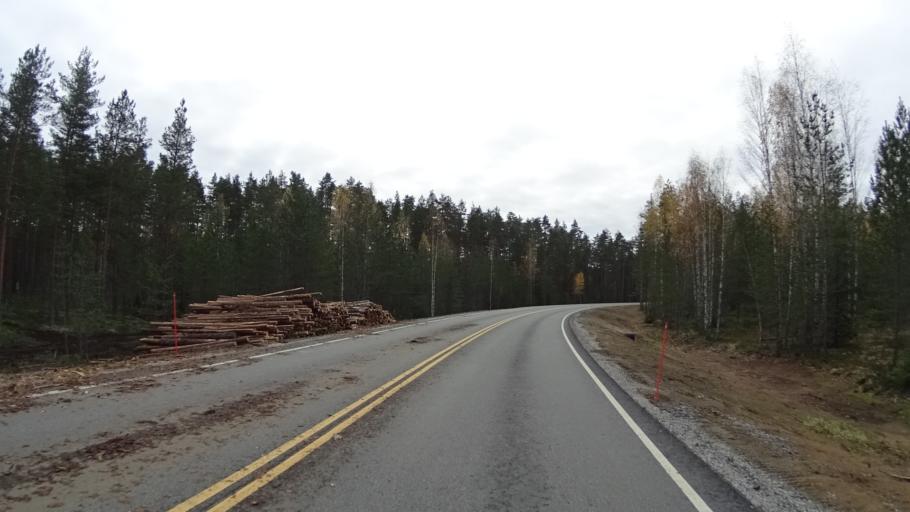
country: FI
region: South Karelia
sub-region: Lappeenranta
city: Lemi
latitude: 60.9907
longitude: 27.9246
